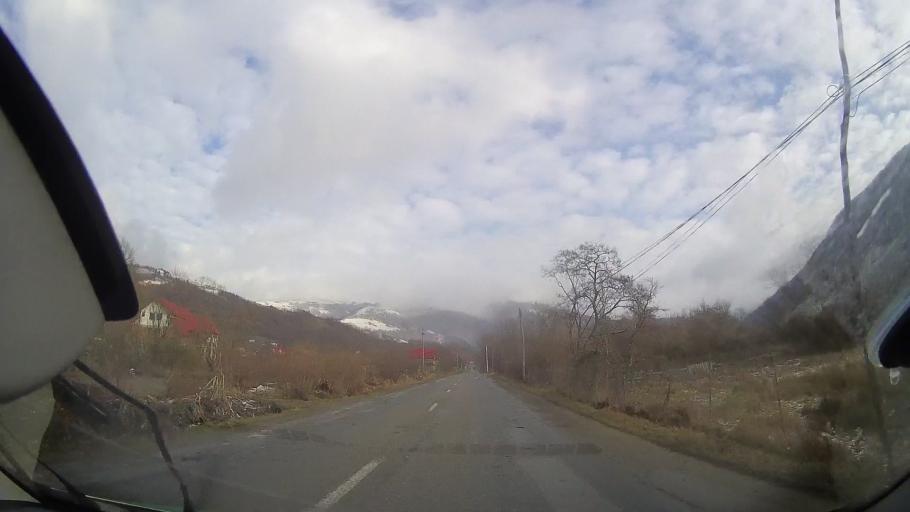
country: RO
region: Alba
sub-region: Comuna Lupsa
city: Lupsa
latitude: 46.3734
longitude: 23.2128
